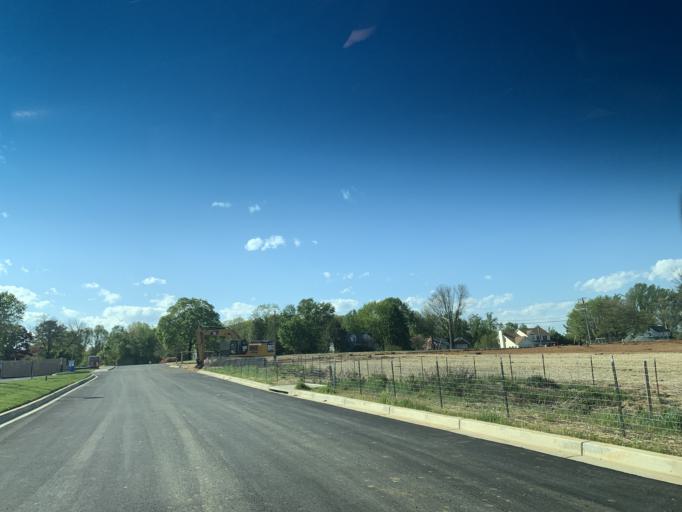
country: US
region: Maryland
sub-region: Harford County
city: Aberdeen
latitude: 39.5299
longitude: -76.1940
